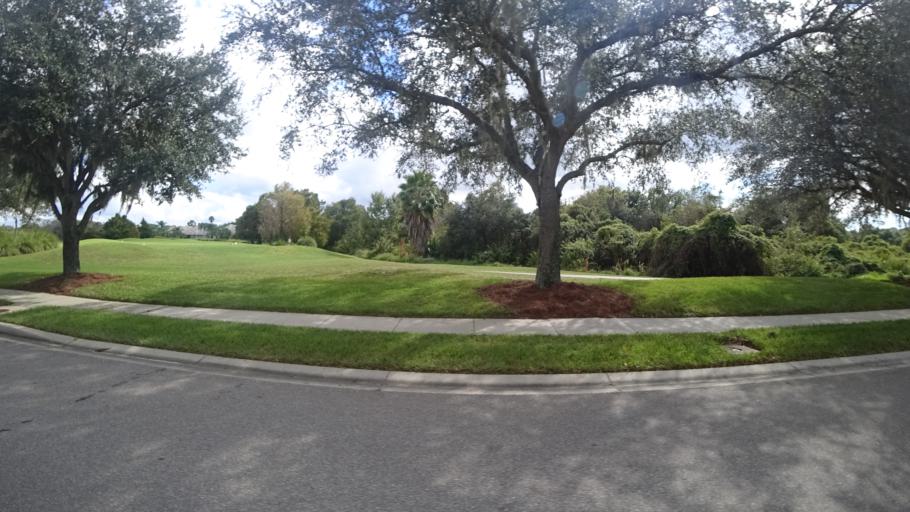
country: US
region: Florida
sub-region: Sarasota County
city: The Meadows
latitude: 27.4021
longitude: -82.4288
